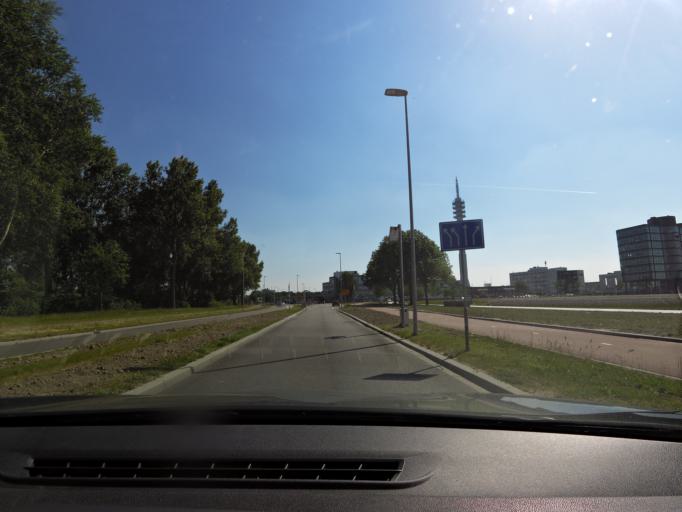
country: NL
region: South Holland
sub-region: Gemeente Rotterdam
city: Delfshaven
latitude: 51.8797
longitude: 4.4541
